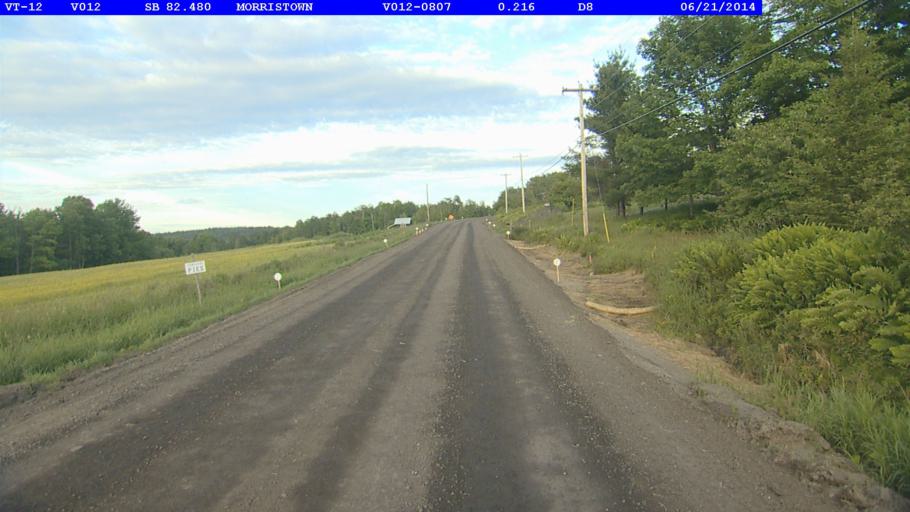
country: US
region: Vermont
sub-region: Lamoille County
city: Morrisville
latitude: 44.5536
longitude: -72.5444
